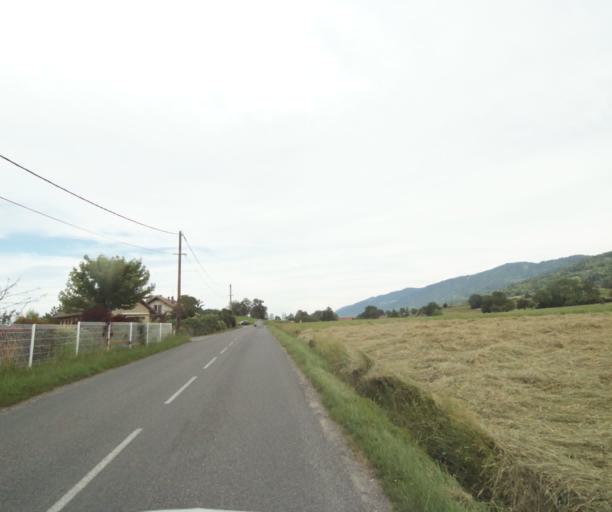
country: FR
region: Rhone-Alpes
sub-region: Departement de la Haute-Savoie
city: Bons-en-Chablais
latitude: 46.2660
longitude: 6.3909
